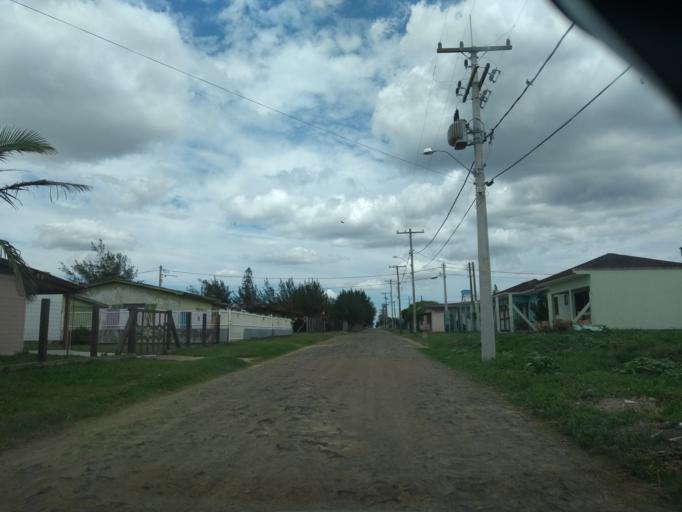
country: BR
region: Rio Grande do Sul
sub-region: Tramandai
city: Tramandai
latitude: -30.0656
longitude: -50.1604
